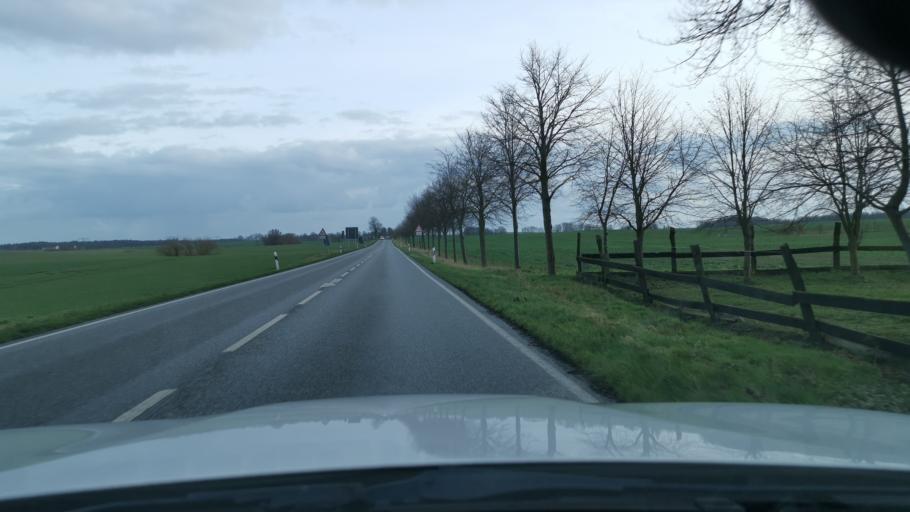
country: DE
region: Mecklenburg-Vorpommern
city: Dummerstorf
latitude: 53.9720
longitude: 12.2863
